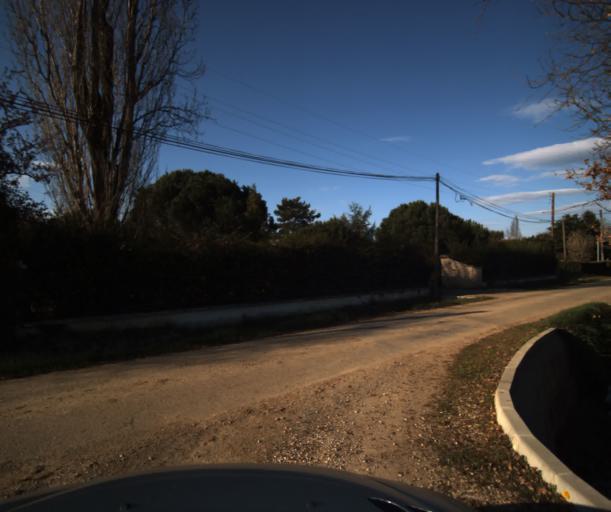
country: FR
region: Midi-Pyrenees
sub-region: Departement du Tarn-et-Garonne
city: Bressols
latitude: 43.9594
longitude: 1.3262
